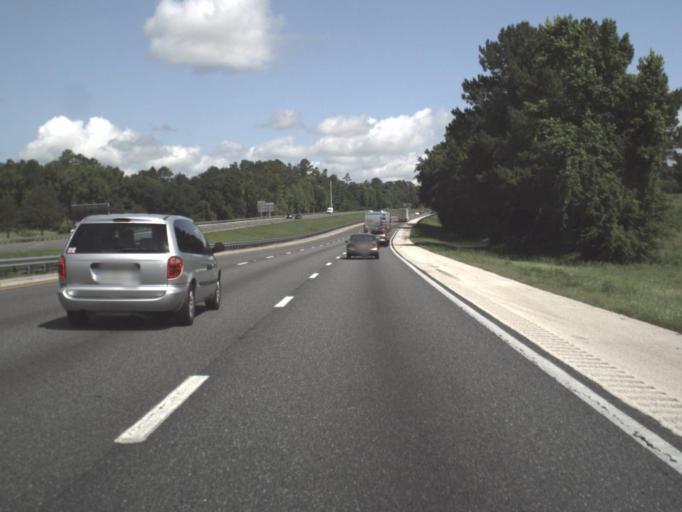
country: US
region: Florida
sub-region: Alachua County
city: Alachua
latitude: 29.6968
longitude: -82.4539
